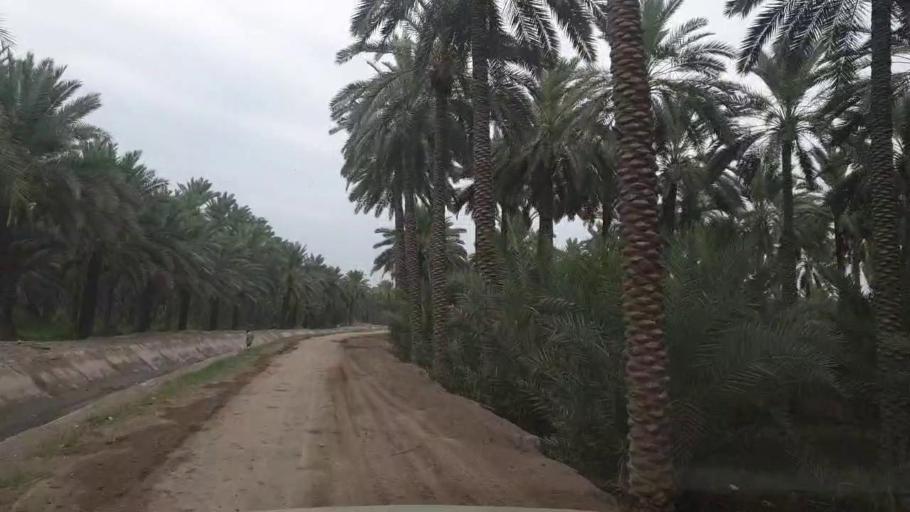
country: PK
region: Sindh
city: Khairpur
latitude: 27.6013
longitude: 68.8019
